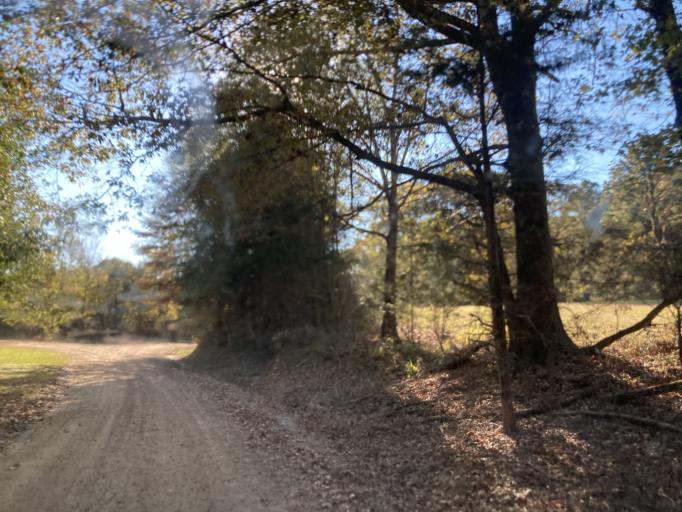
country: US
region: Mississippi
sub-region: Yazoo County
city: Yazoo City
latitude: 32.7393
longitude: -90.4391
